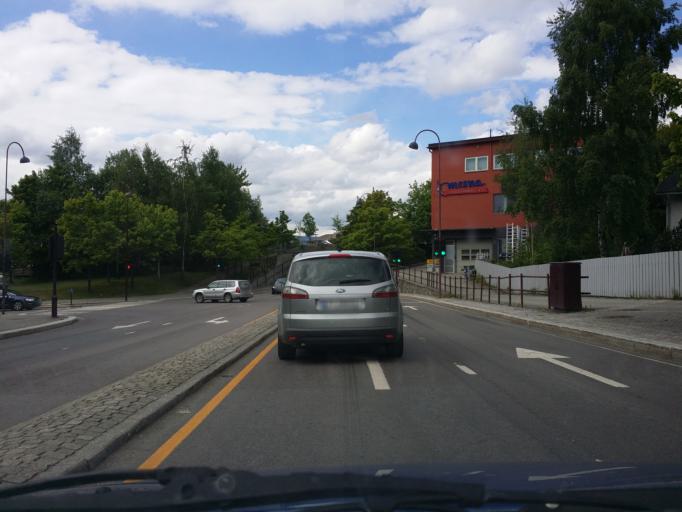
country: NO
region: Oppland
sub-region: Lillehammer
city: Lillehammer
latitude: 61.1133
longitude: 10.4642
